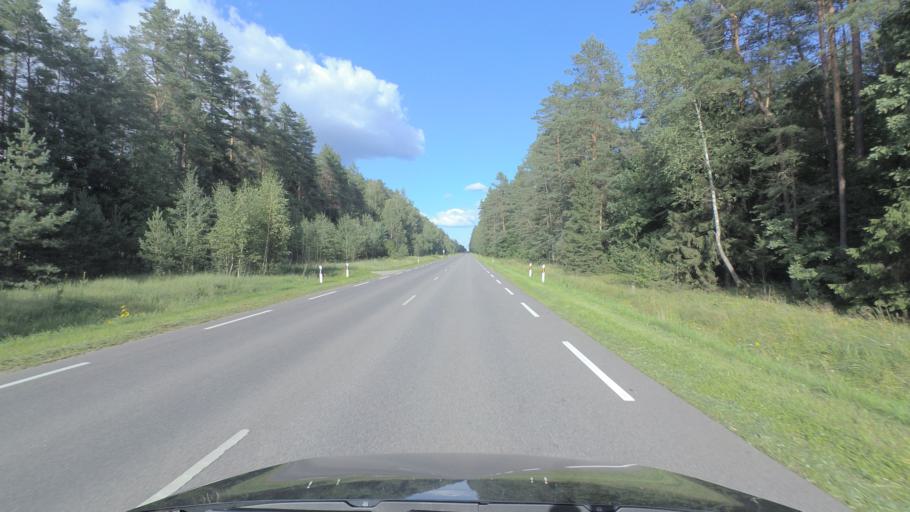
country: LT
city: Pabrade
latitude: 54.9684
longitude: 25.7210
